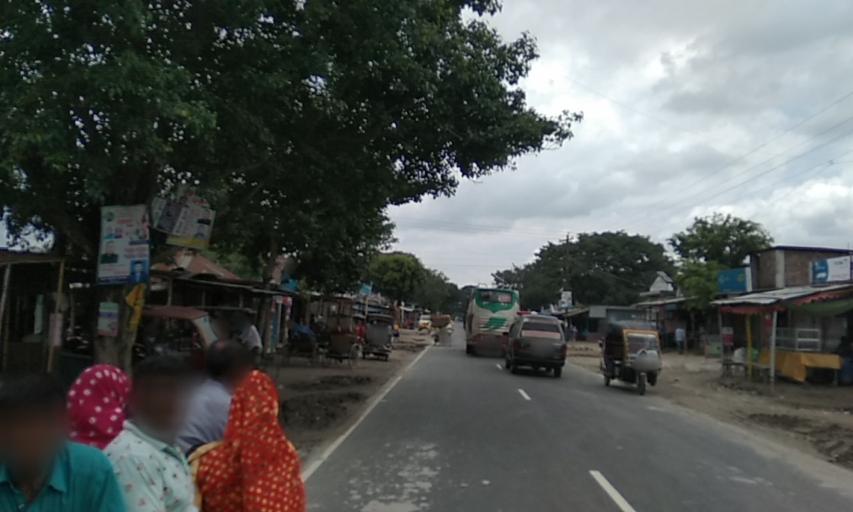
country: BD
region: Rangpur Division
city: Rangpur
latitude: 25.7992
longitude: 89.1919
